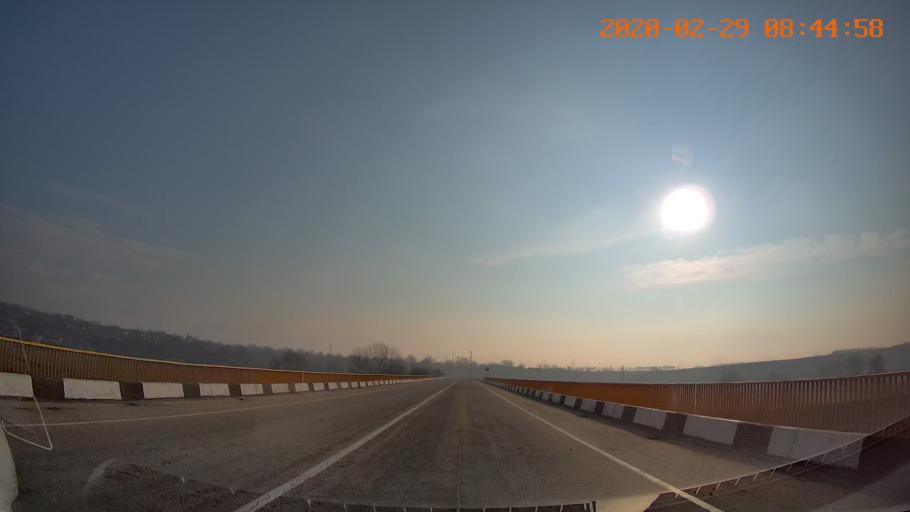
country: MD
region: Anenii Noi
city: Varnita
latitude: 46.9198
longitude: 29.4727
